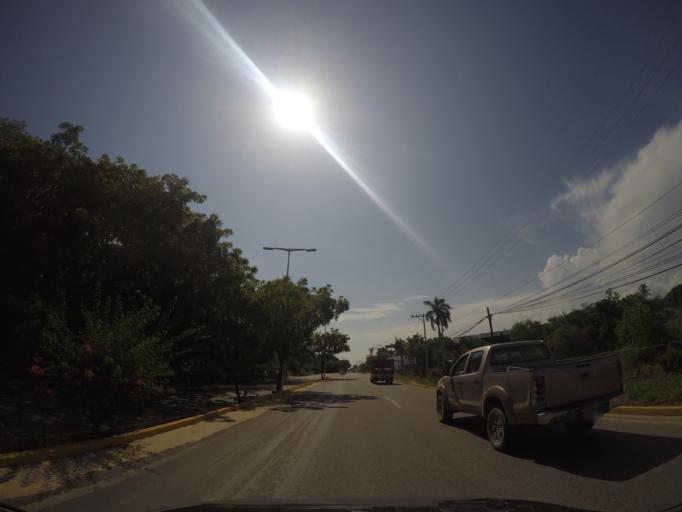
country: MX
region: Oaxaca
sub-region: San Pedro Mixtepec -Dto. 22 -
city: Puerto Escondido
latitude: 15.8699
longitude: -97.0863
